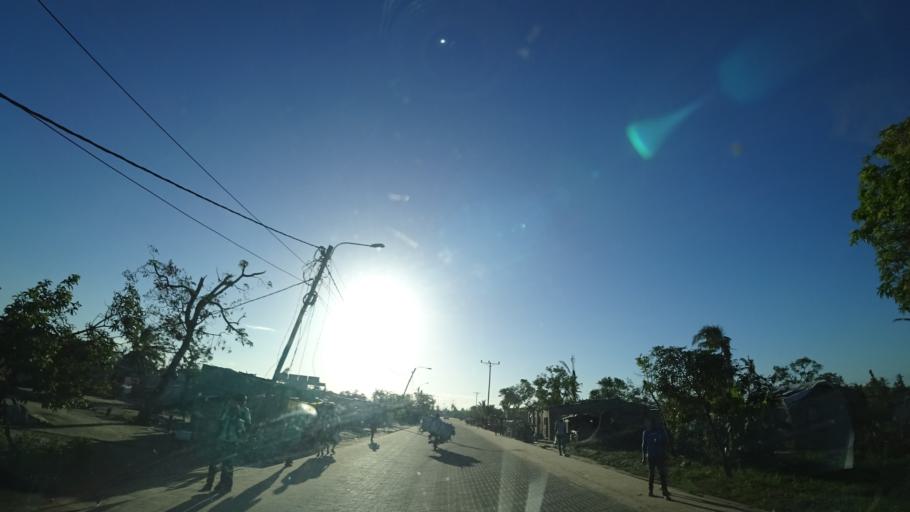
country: MZ
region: Sofala
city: Beira
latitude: -19.7447
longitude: 34.8451
